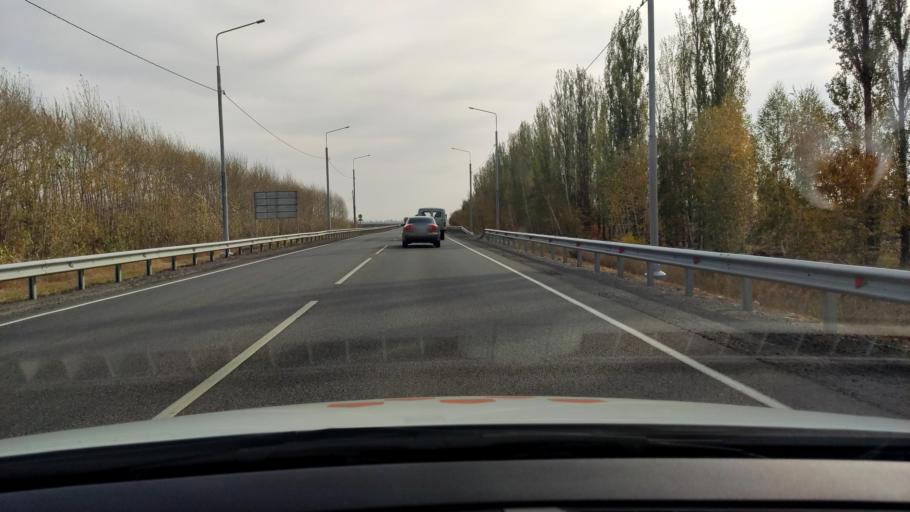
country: RU
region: Voronezj
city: Volya
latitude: 51.6890
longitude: 39.5063
